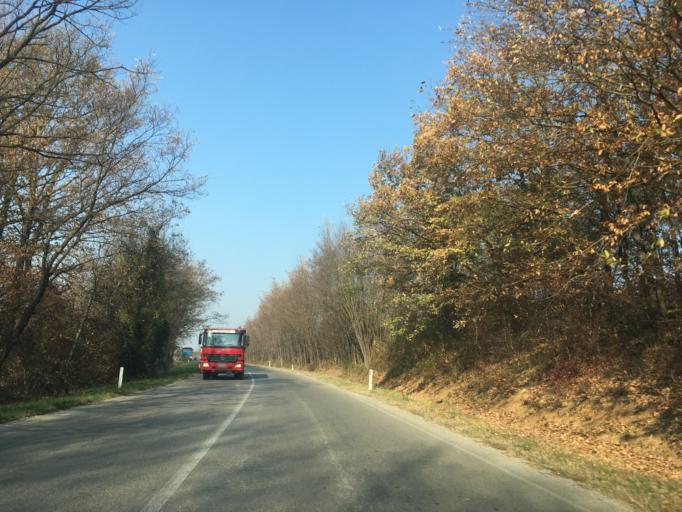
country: XK
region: Pec
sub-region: Komuna e Pejes
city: Dubova (Driloni)
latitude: 42.6467
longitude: 20.4116
